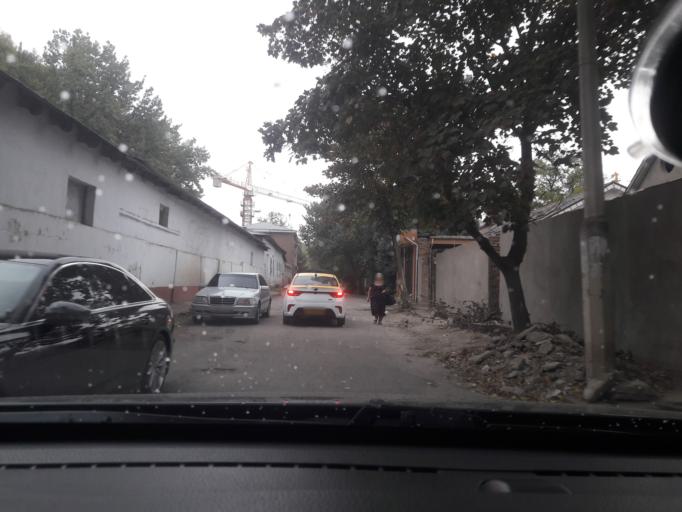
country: TJ
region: Dushanbe
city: Dushanbe
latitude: 38.5649
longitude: 68.7912
